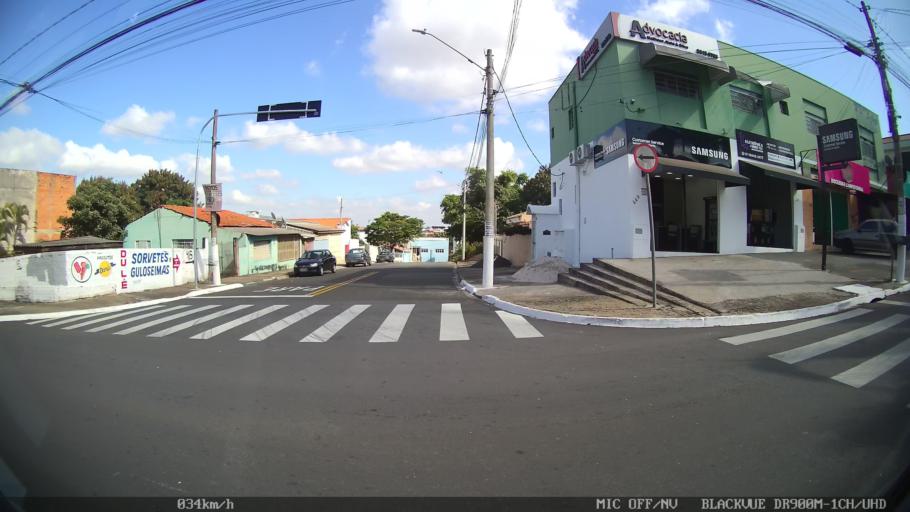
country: BR
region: Sao Paulo
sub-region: Hortolandia
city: Hortolandia
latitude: -22.8555
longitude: -47.2161
